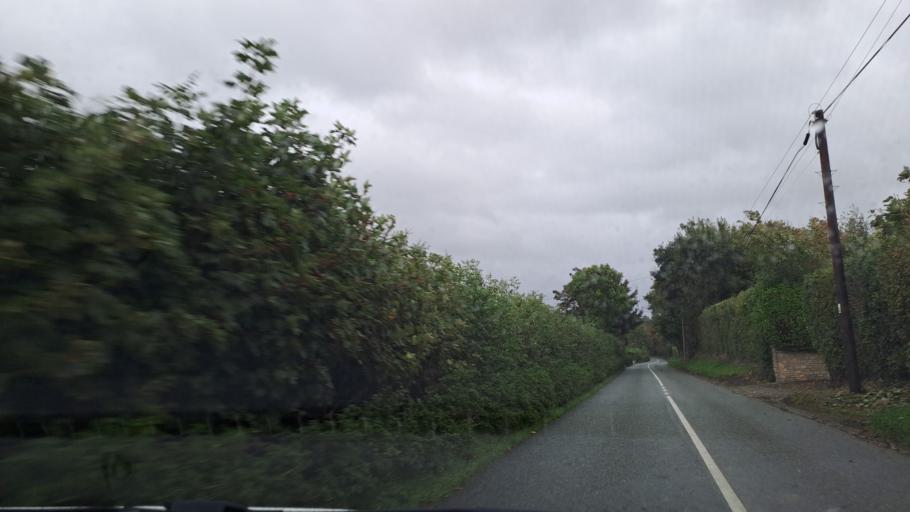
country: IE
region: Leinster
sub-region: Lu
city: Dromiskin
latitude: 53.9586
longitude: -6.4425
